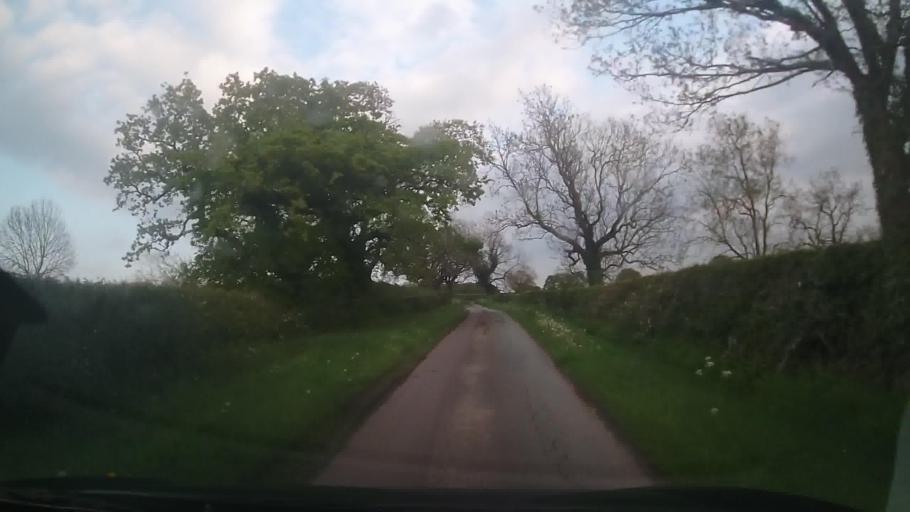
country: GB
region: England
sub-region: Shropshire
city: Ellesmere
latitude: 52.9423
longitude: -2.8653
